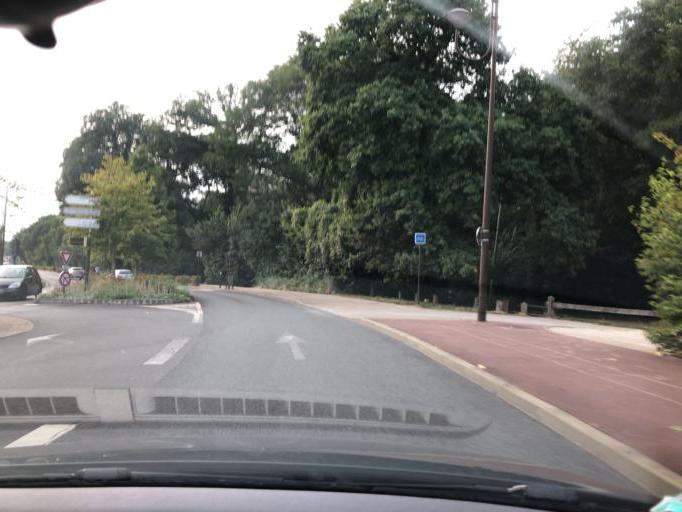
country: FR
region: Ile-de-France
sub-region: Departement des Yvelines
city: Velizy-Villacoublay
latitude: 48.7868
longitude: 2.1869
